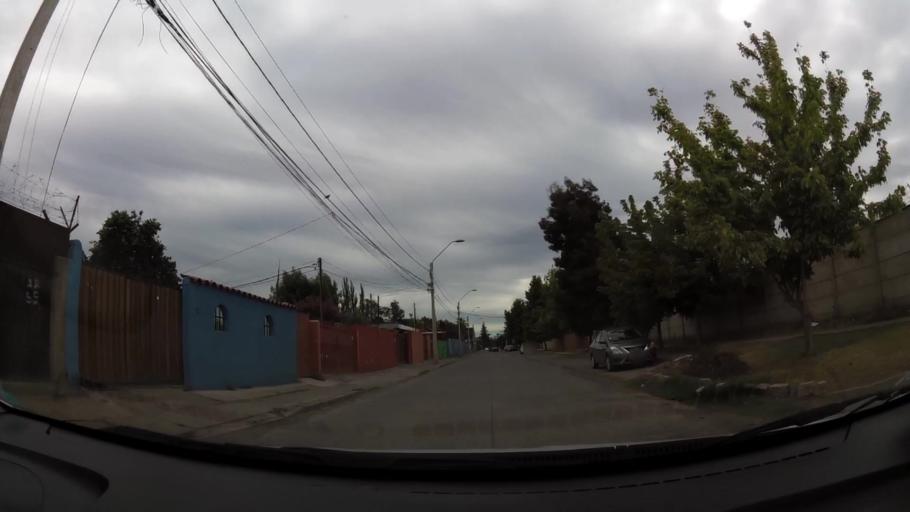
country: CL
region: O'Higgins
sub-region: Provincia de Cachapoal
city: Rancagua
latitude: -34.1652
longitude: -70.7300
